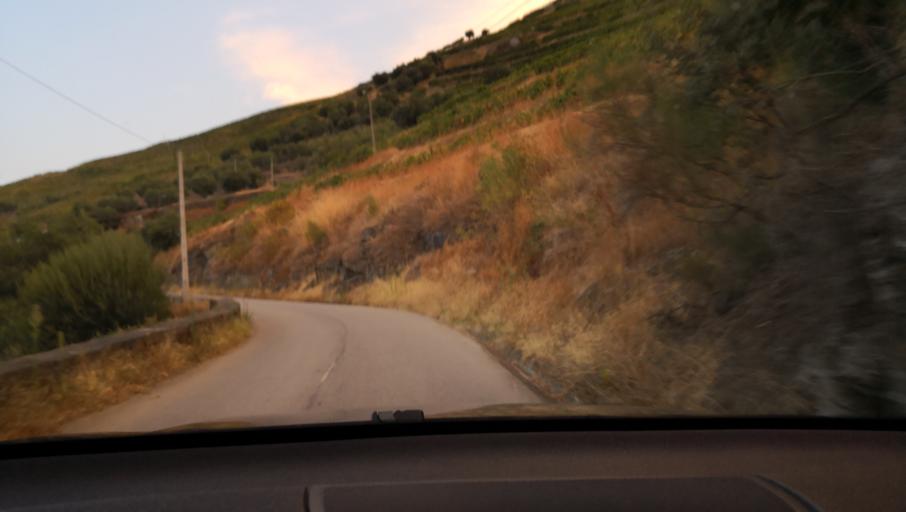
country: PT
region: Vila Real
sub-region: Peso da Regua
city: Peso da Regua
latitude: 41.1796
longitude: -7.7557
